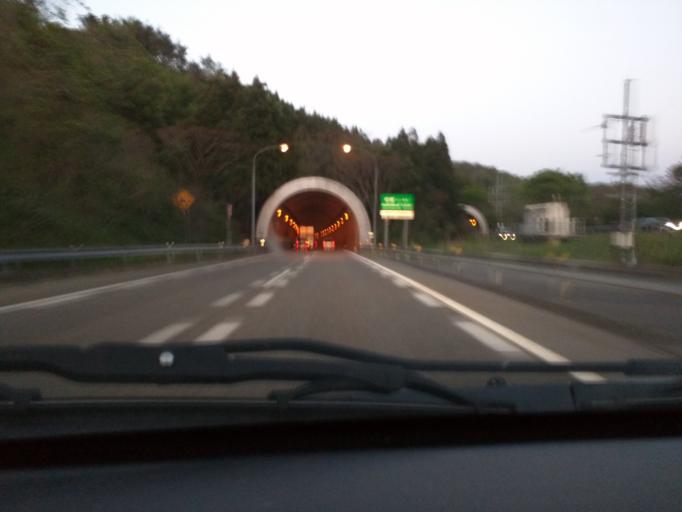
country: JP
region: Niigata
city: Kashiwazaki
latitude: 37.3382
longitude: 138.5356
